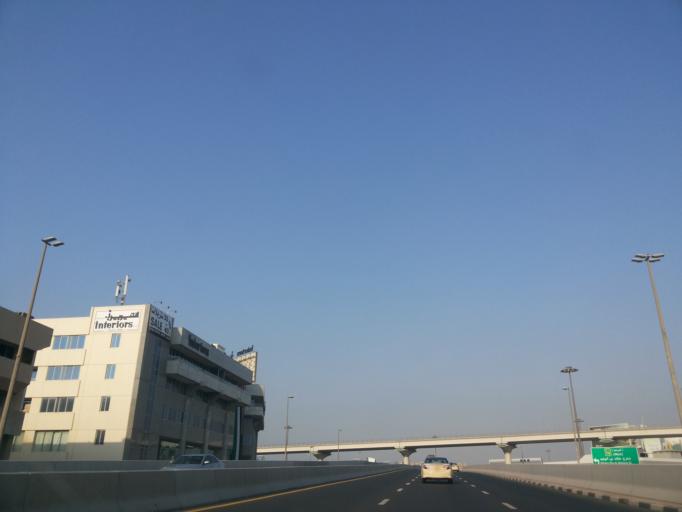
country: AE
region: Ash Shariqah
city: Sharjah
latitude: 25.2465
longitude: 55.3133
